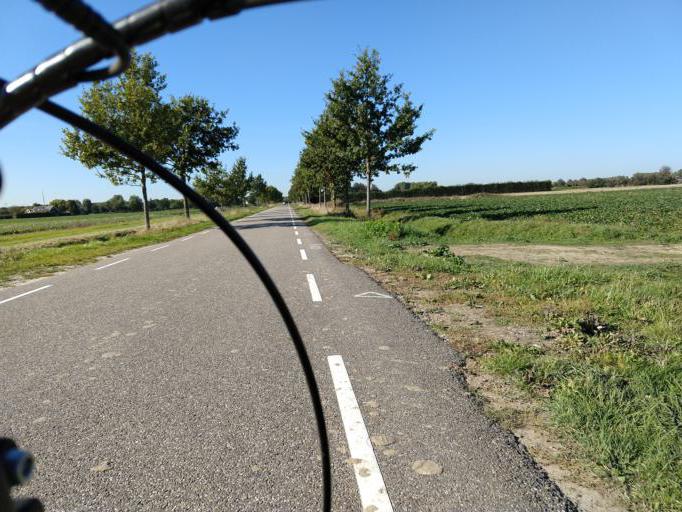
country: NL
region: Zeeland
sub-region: Gemeente Terneuzen
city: Terneuzen
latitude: 51.4228
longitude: 3.8328
